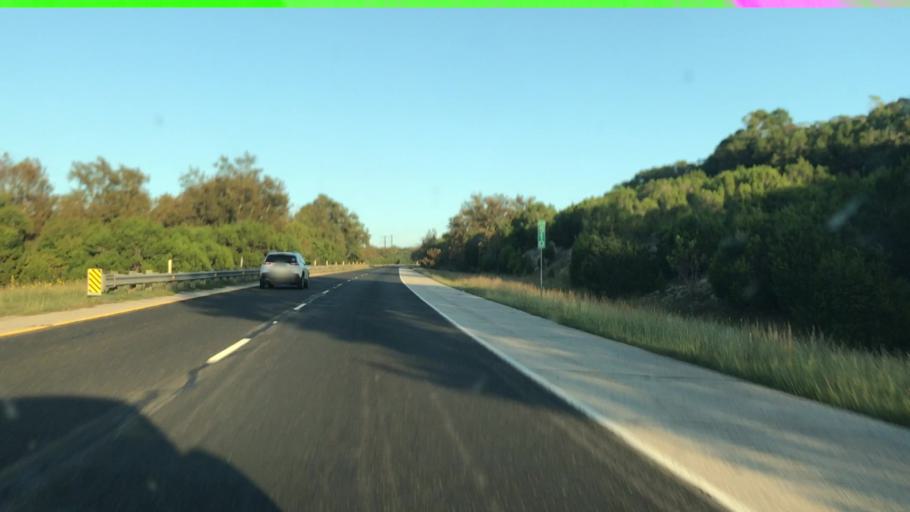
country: US
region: Texas
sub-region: Kerr County
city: Kerrville
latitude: 30.0694
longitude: -99.0841
